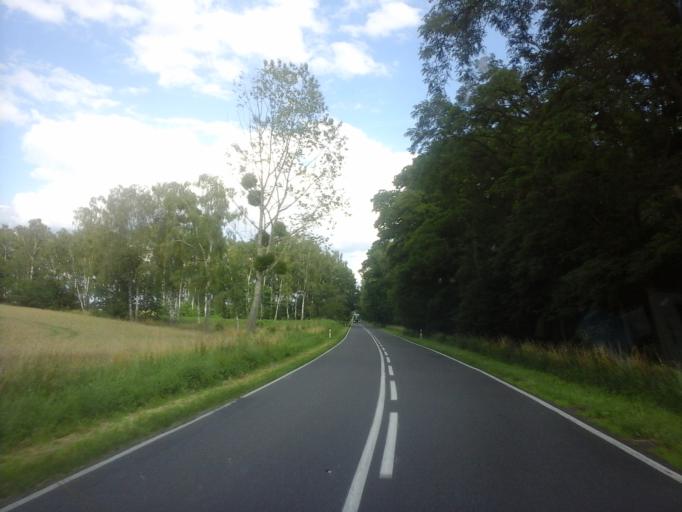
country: PL
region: West Pomeranian Voivodeship
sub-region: Powiat stargardzki
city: Suchan
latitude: 53.2002
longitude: 15.3429
